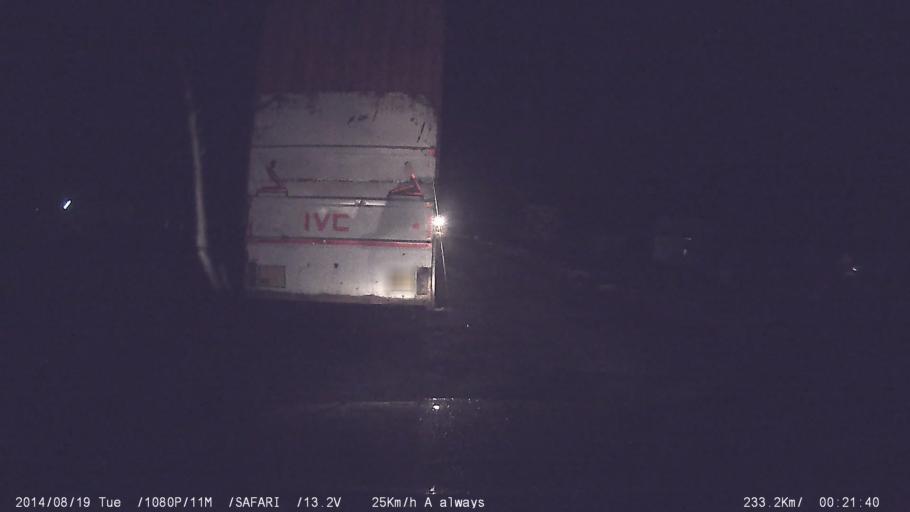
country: IN
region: Kerala
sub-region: Palakkad district
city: Palakkad
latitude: 10.7974
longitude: 76.7426
